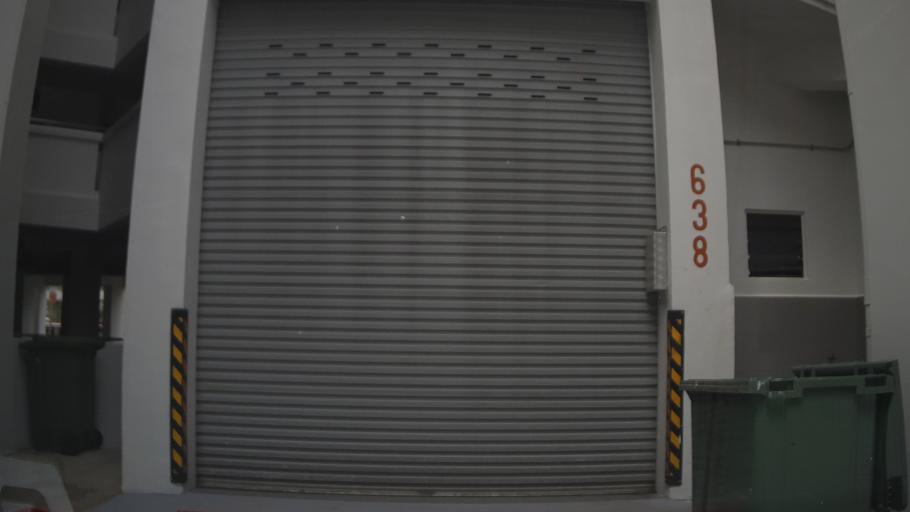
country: MY
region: Johor
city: Johor Bahru
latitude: 1.3974
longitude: 103.7484
